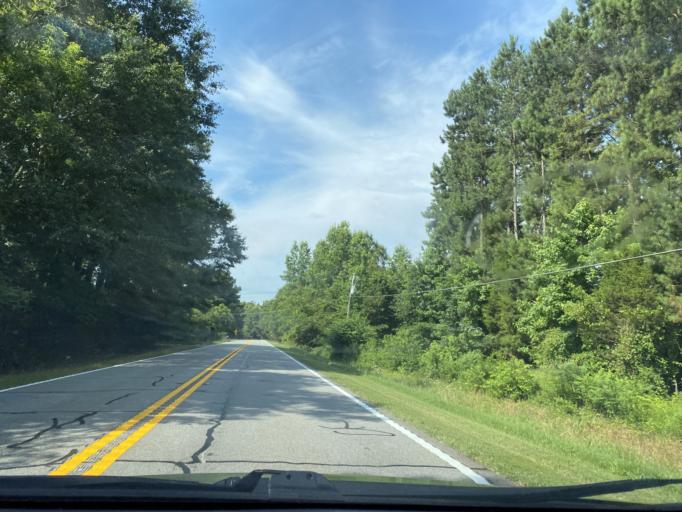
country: US
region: Georgia
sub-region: Coweta County
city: Grantville
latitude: 33.2517
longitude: -84.7269
